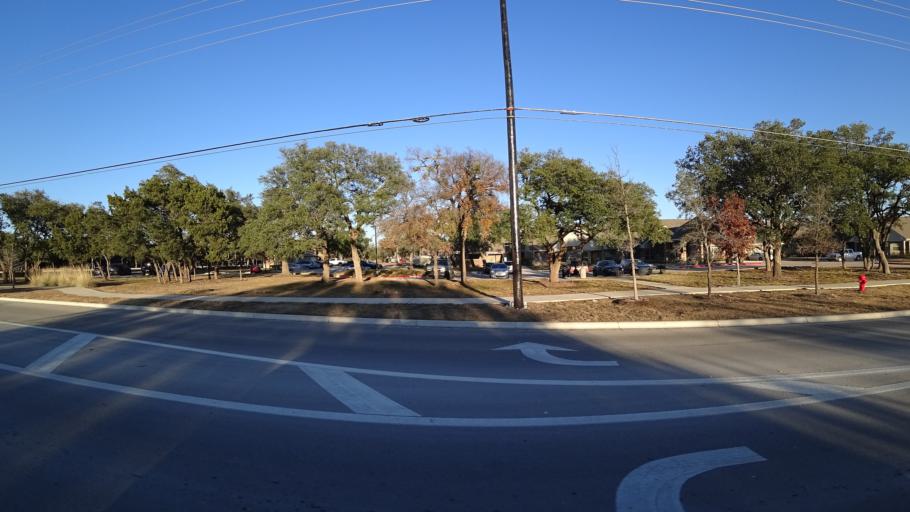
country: US
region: Texas
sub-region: Williamson County
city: Cedar Park
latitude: 30.5356
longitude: -97.8087
